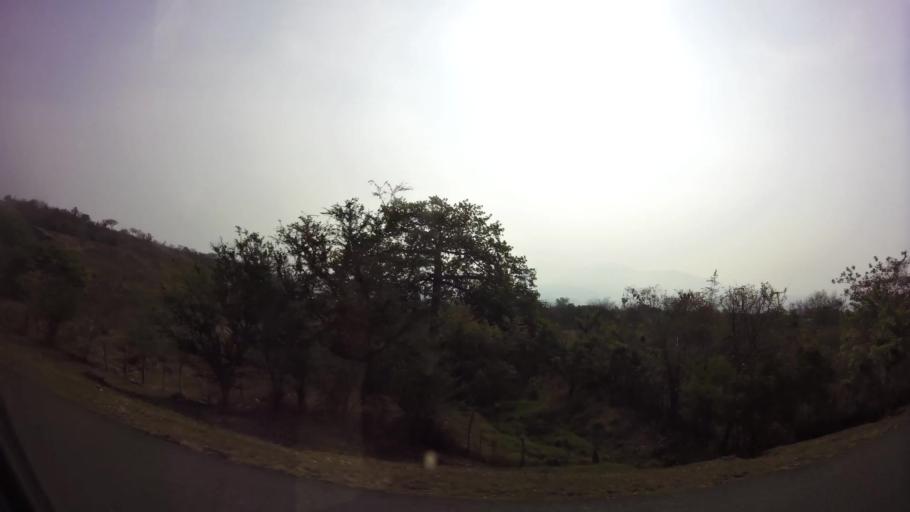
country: HN
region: Comayagua
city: Comayagua
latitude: 14.4490
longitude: -87.6626
